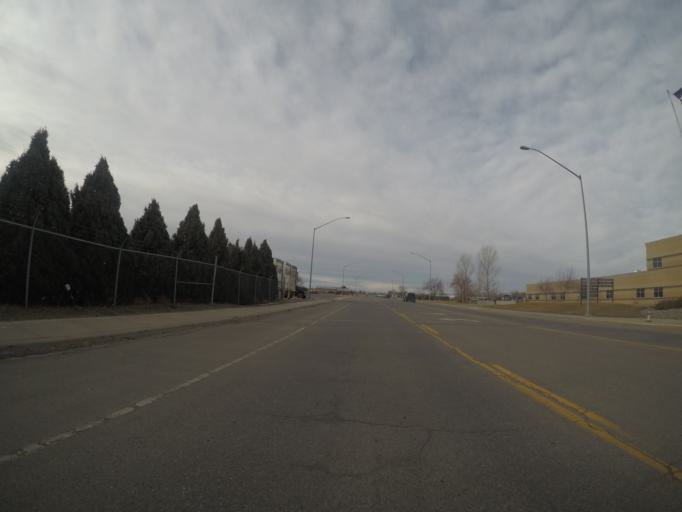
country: US
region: Montana
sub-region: Yellowstone County
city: Billings
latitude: 45.7443
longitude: -108.5891
